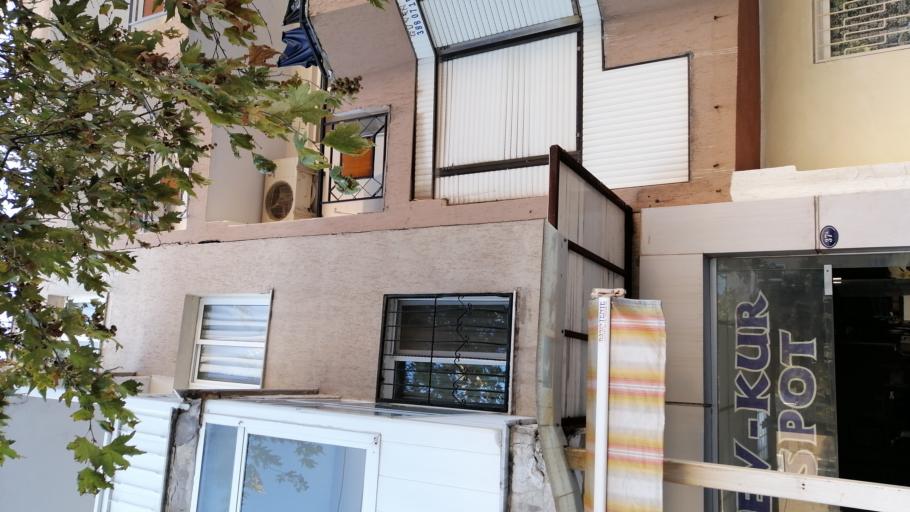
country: TR
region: Izmir
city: Bornova
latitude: 38.4570
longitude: 27.1964
